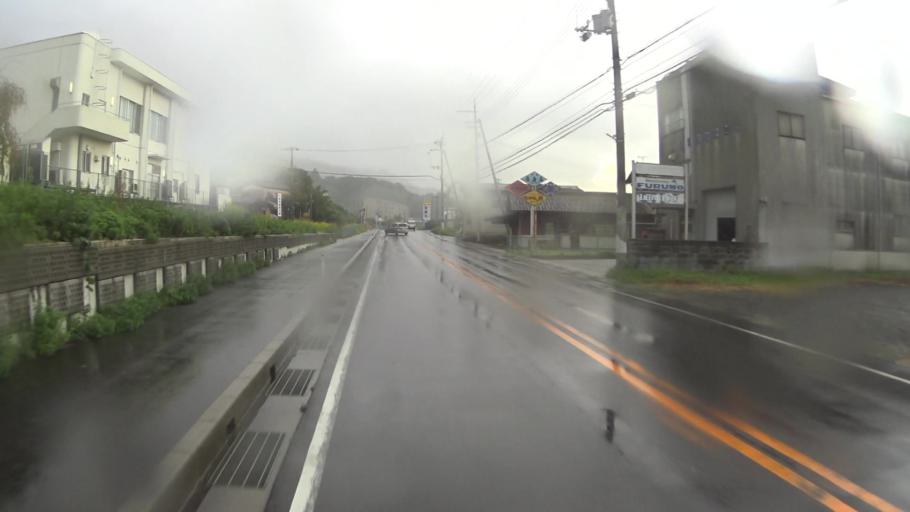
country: JP
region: Kyoto
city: Miyazu
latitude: 35.5458
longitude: 135.2108
